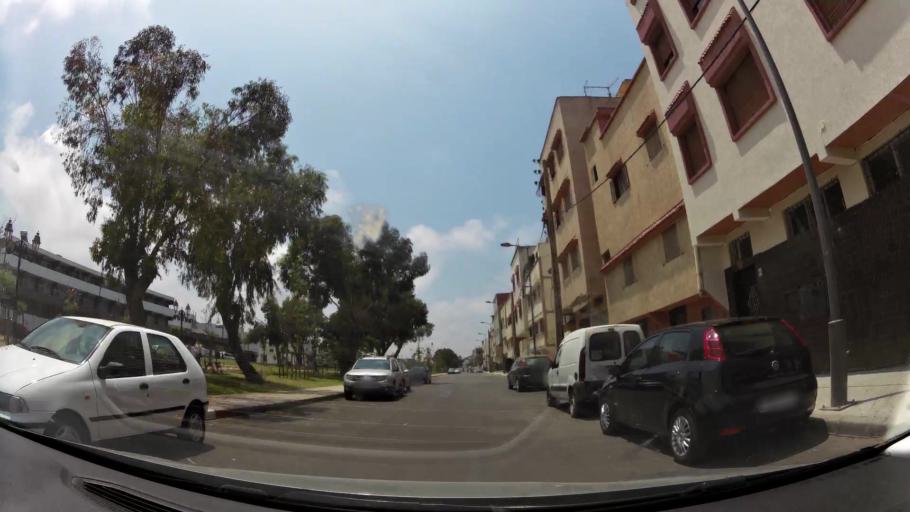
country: MA
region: Rabat-Sale-Zemmour-Zaer
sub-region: Rabat
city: Rabat
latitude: 33.9875
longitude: -6.8733
